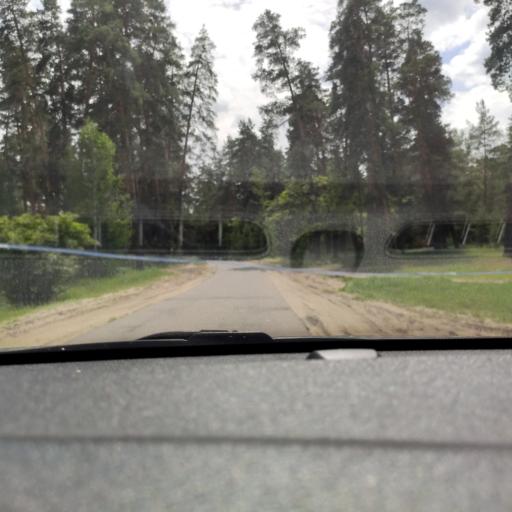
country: RU
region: Voronezj
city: Somovo
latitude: 51.8141
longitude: 39.3269
